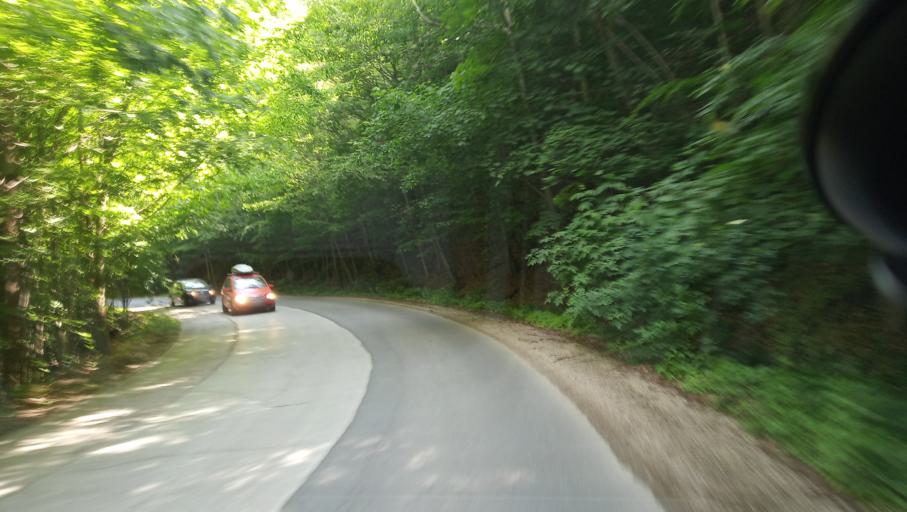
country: RO
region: Cluj
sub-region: Comuna Capusu Mare
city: Capusu Mare
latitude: 46.7098
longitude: 23.2643
